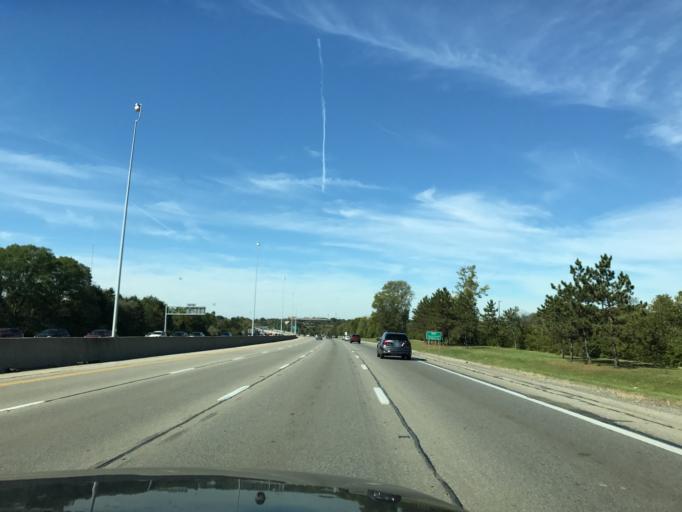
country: US
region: Ohio
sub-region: Franklin County
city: Dublin
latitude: 40.1096
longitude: -83.1014
